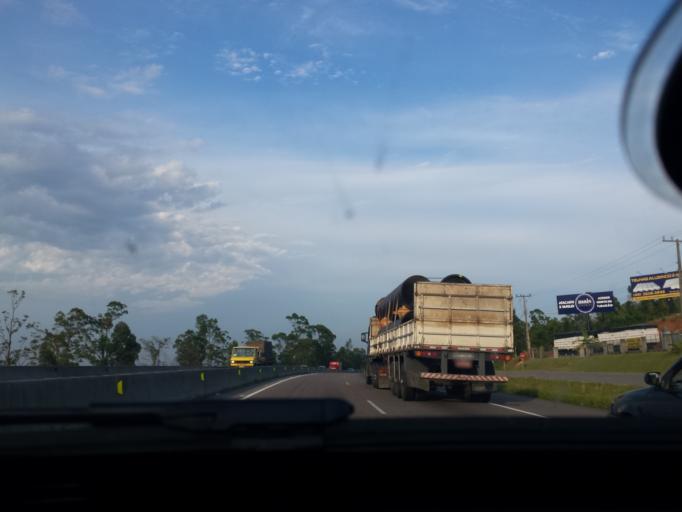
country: BR
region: Santa Catarina
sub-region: Tubarao
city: Tubarao
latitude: -28.4293
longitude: -48.9179
